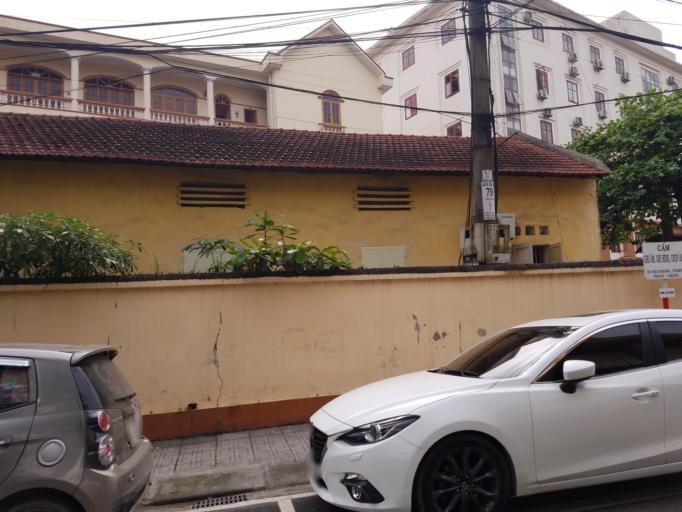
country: VN
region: Thai Nguyen
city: Thanh Pho Thai Nguyen
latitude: 21.5938
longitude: 105.8426
